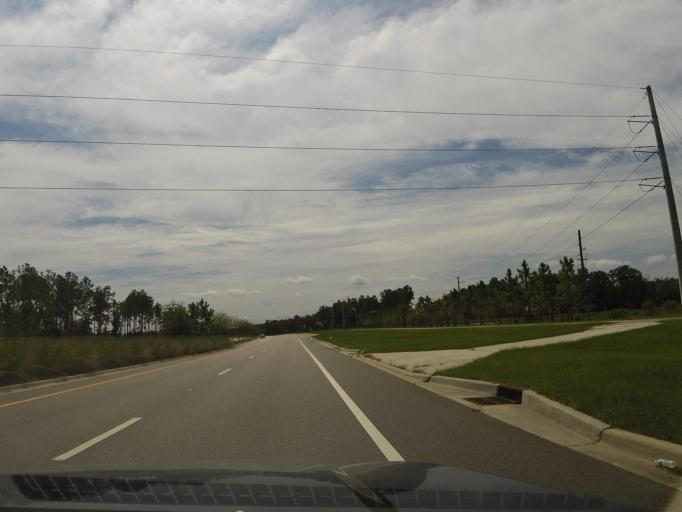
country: US
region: Florida
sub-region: Saint Johns County
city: Fruit Cove
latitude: 30.0367
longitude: -81.5282
